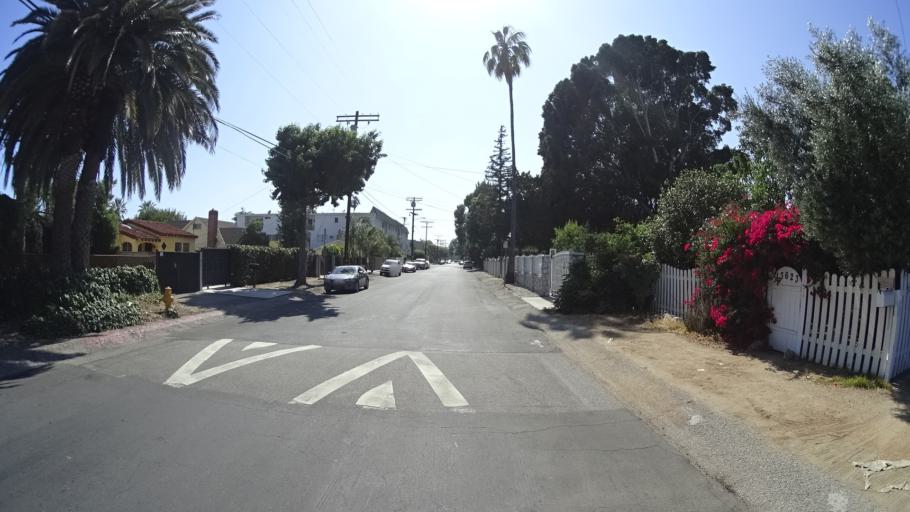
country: US
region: California
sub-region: Los Angeles County
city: Van Nuys
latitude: 34.1976
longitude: -118.4299
